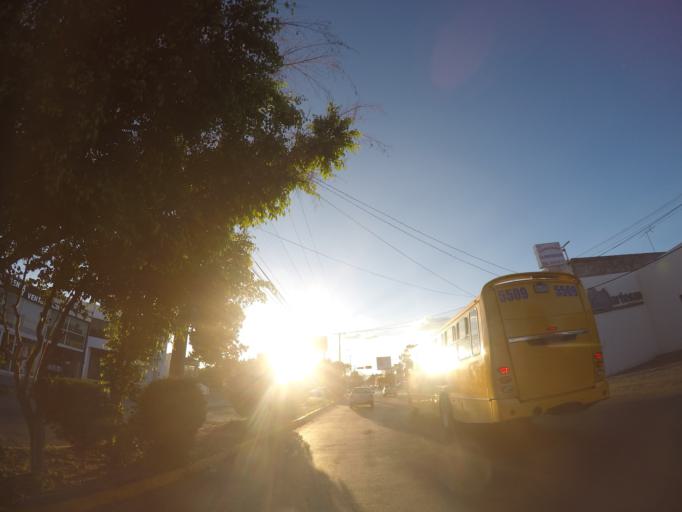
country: MX
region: San Luis Potosi
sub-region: San Luis Potosi
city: San Luis Potosi
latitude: 22.1437
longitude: -101.0021
